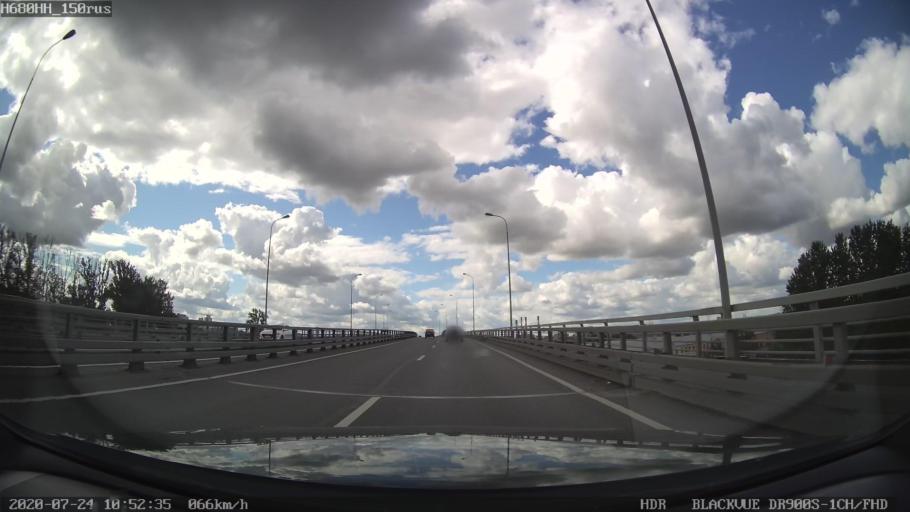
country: RU
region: St.-Petersburg
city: Admiralteisky
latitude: 59.8850
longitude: 30.3013
